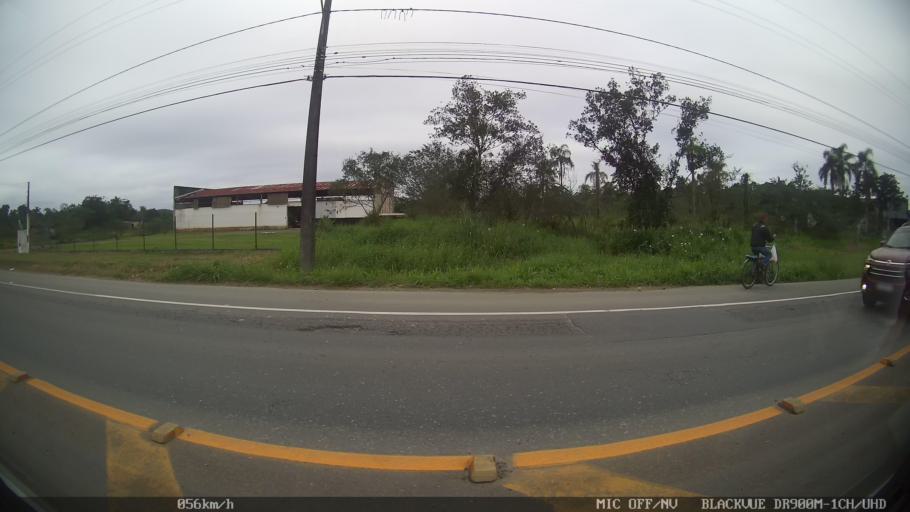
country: BR
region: Santa Catarina
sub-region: Joinville
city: Joinville
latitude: -26.3103
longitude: -48.9219
